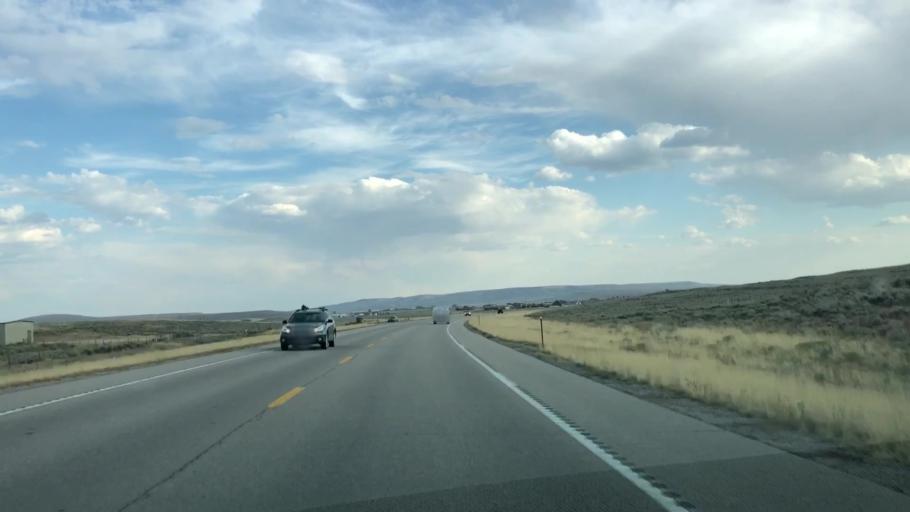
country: US
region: Wyoming
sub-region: Sublette County
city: Pinedale
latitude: 42.9975
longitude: -110.0952
